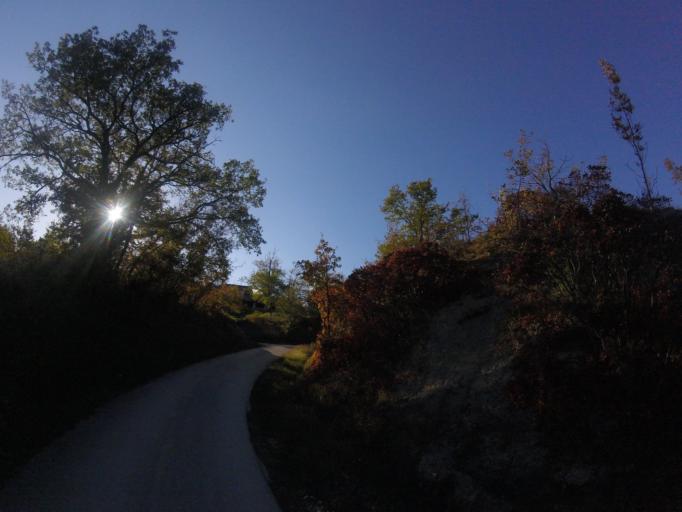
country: HR
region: Istarska
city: Pazin
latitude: 45.2225
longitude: 14.0449
